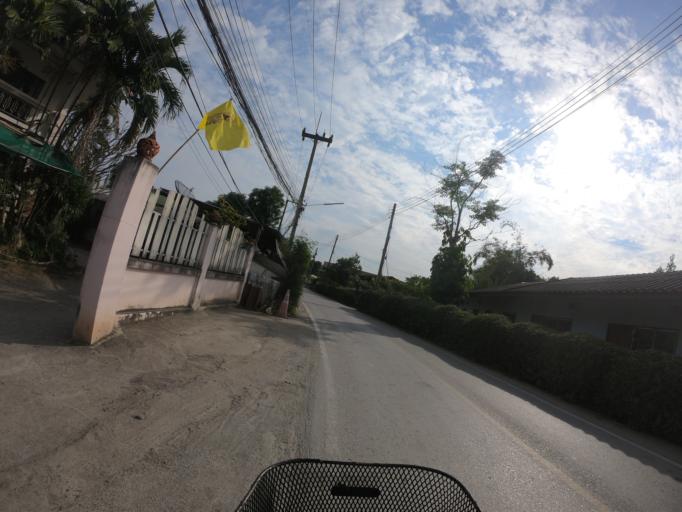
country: TH
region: Chiang Mai
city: Saraphi
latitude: 18.7415
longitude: 99.0433
